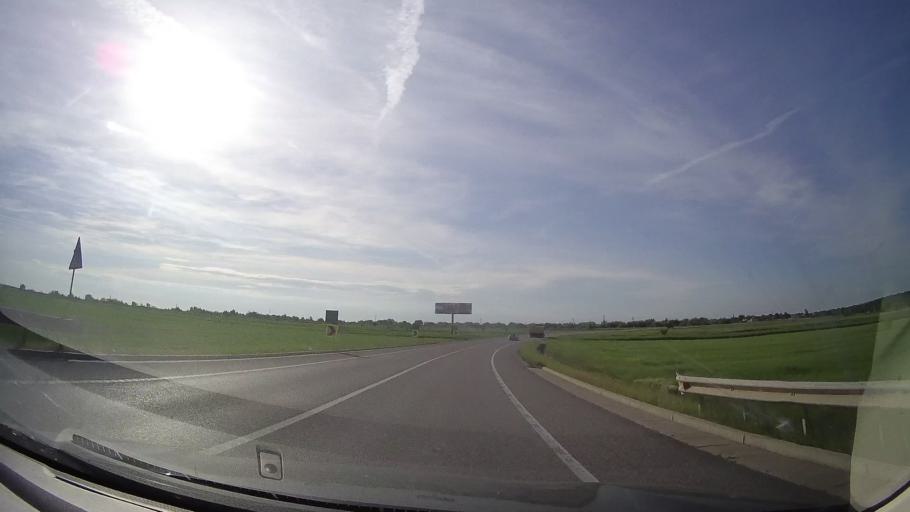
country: RO
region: Timis
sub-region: Comuna Costeiu
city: Costeiu
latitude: 45.7219
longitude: 21.8722
